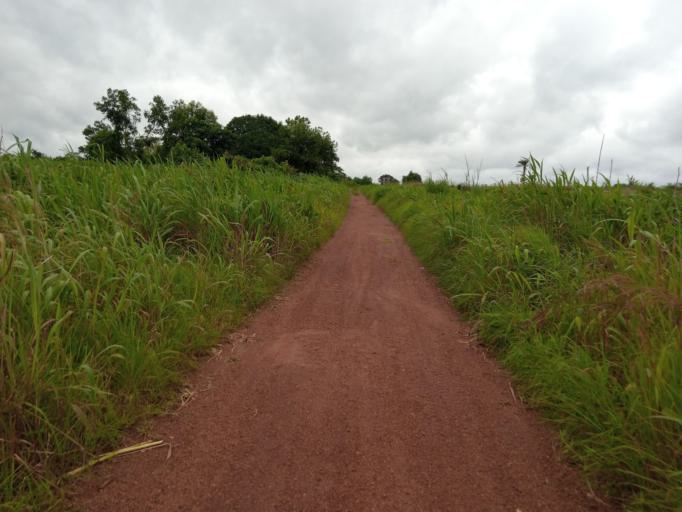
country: SL
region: Southern Province
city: Largo
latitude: 8.1983
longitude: -12.0505
